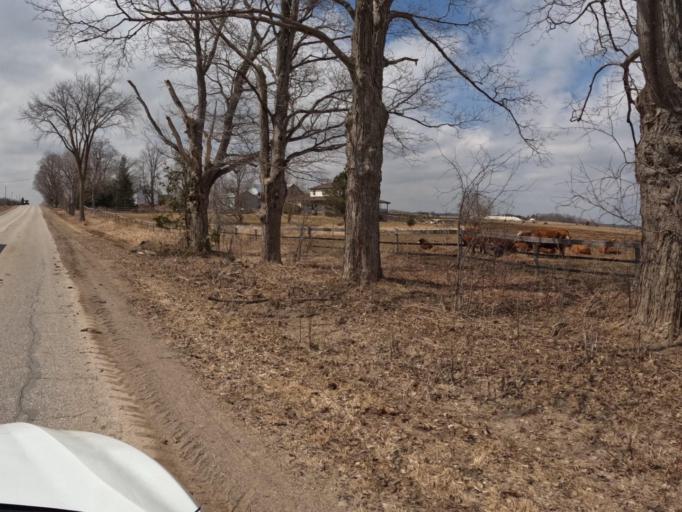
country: CA
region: Ontario
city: Shelburne
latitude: 44.0182
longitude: -80.1669
